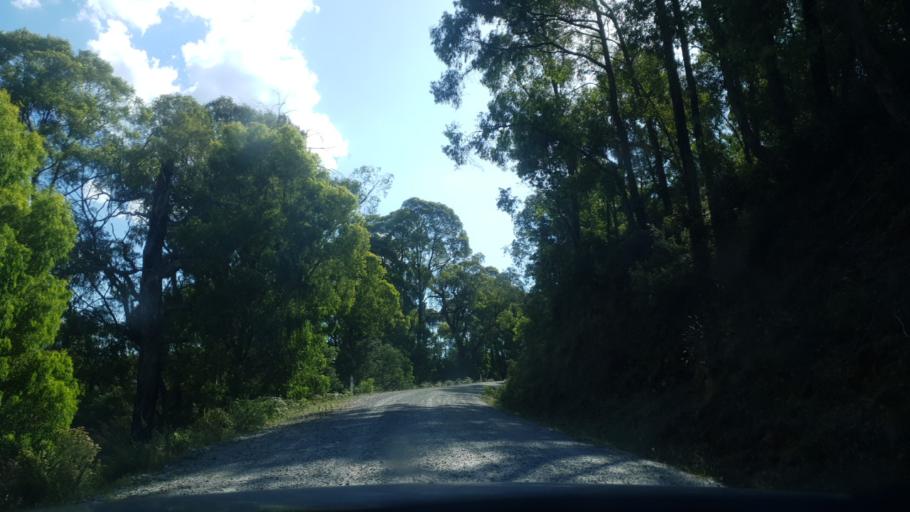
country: AU
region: Victoria
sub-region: Alpine
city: Mount Beauty
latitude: -36.7507
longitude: 147.1856
